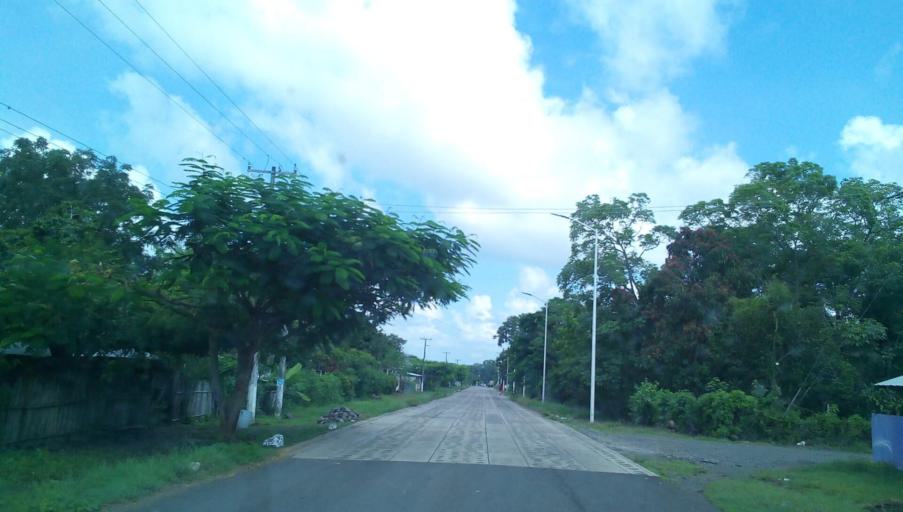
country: MX
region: Veracruz
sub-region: Citlaltepetl
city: Las Sabinas
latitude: 21.3595
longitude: -97.9001
